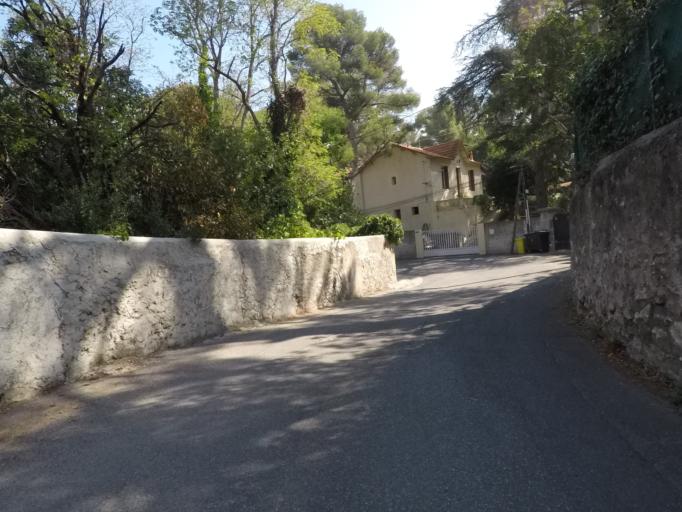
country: FR
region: Provence-Alpes-Cote d'Azur
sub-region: Departement des Bouches-du-Rhone
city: Marseille 09
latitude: 43.2556
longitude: 5.4354
